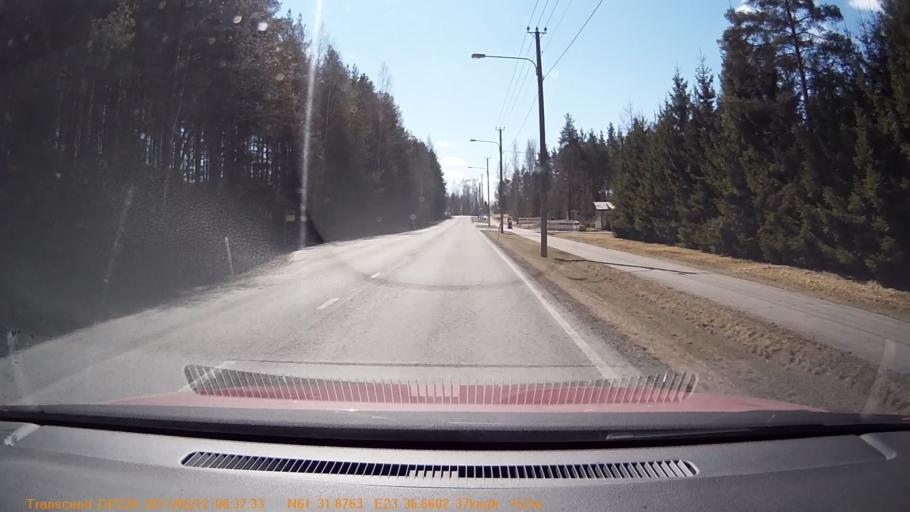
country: FI
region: Pirkanmaa
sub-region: Tampere
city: Yloejaervi
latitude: 61.5313
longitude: 23.6110
